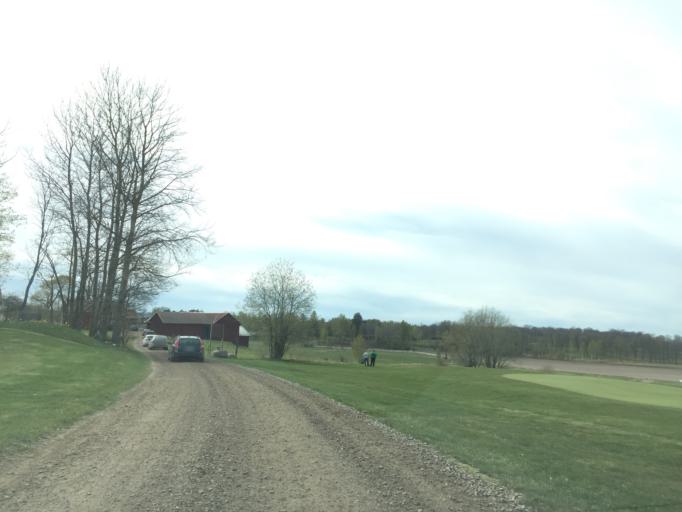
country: SE
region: OErebro
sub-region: Lekebergs Kommun
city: Fjugesta
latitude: 59.0541
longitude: 14.9088
